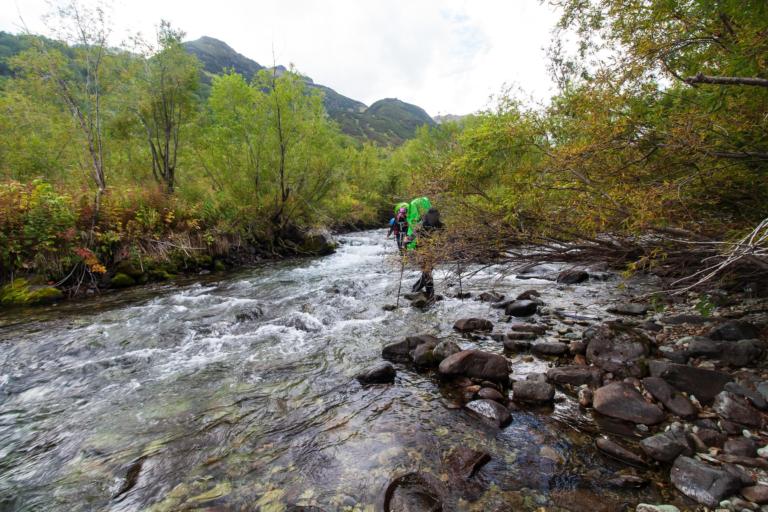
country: RU
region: Kamtsjatka
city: Yelizovo
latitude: 53.8320
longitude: 158.3235
